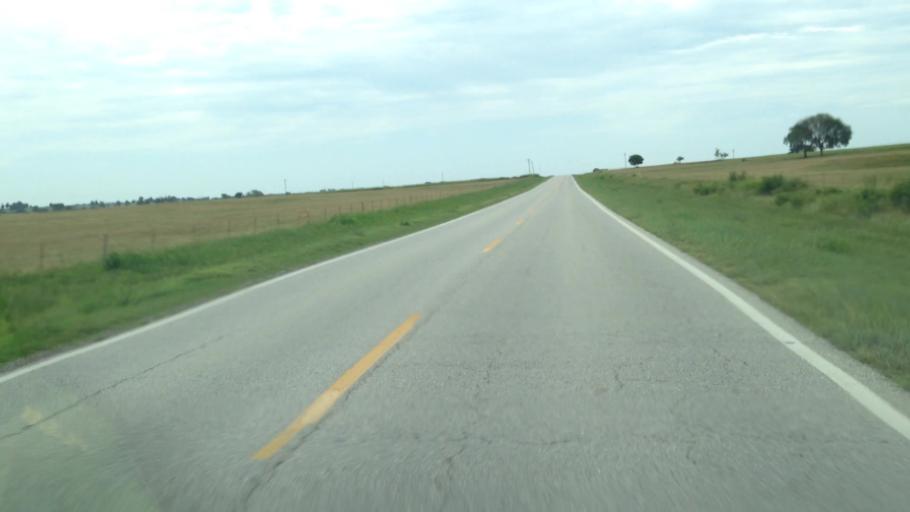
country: US
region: Kansas
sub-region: Labette County
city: Chetopa
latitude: 36.8410
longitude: -95.1284
